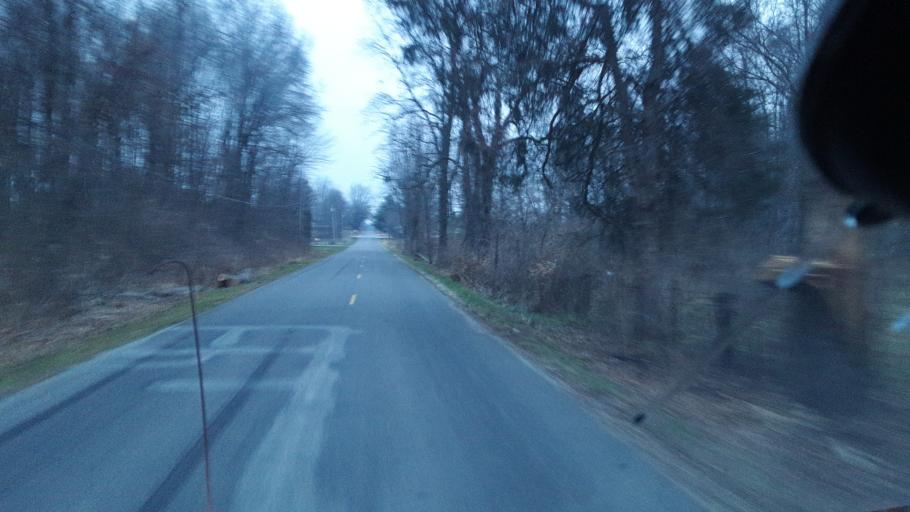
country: US
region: Indiana
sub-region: Elkhart County
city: Bristol
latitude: 41.6646
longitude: -85.7873
